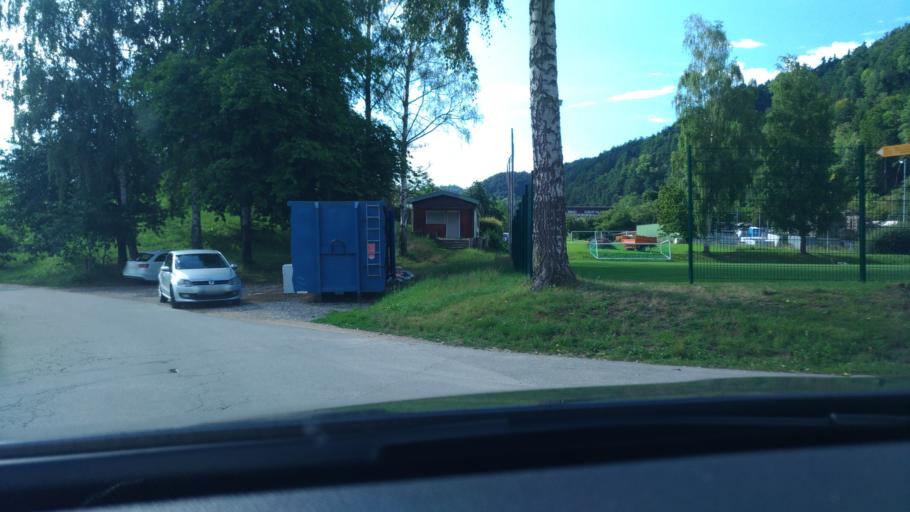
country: DE
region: Baden-Wuerttemberg
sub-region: Tuebingen Region
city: Sipplingen
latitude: 47.7957
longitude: 9.1084
